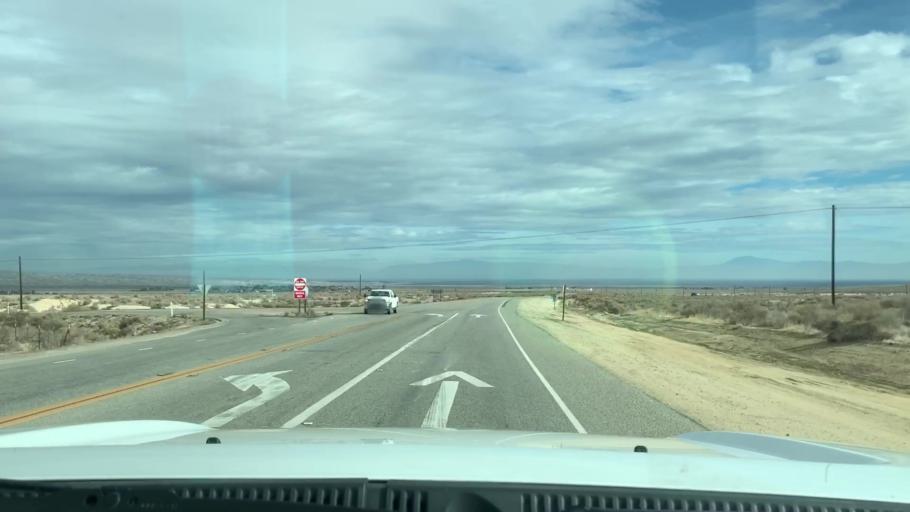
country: US
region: California
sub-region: Kern County
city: Ford City
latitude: 35.1865
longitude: -119.4463
